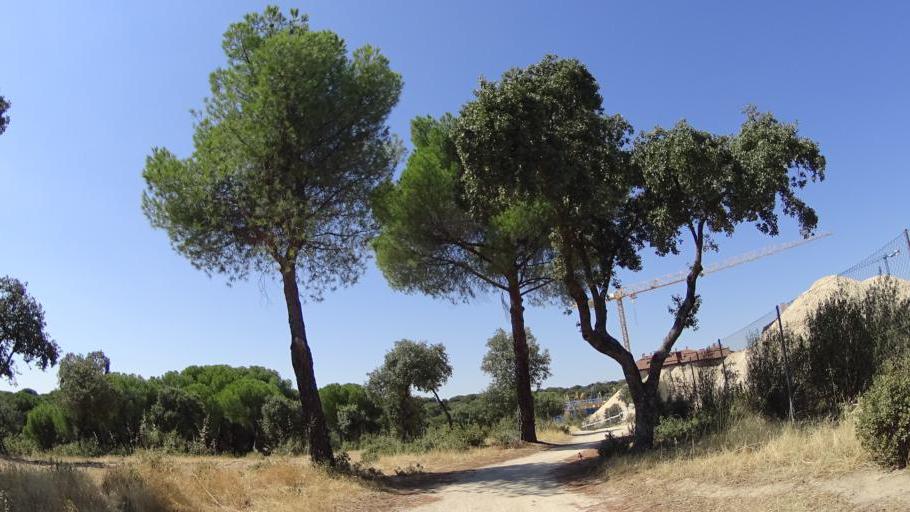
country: ES
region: Madrid
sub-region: Provincia de Madrid
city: Majadahonda
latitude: 40.4406
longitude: -3.8705
